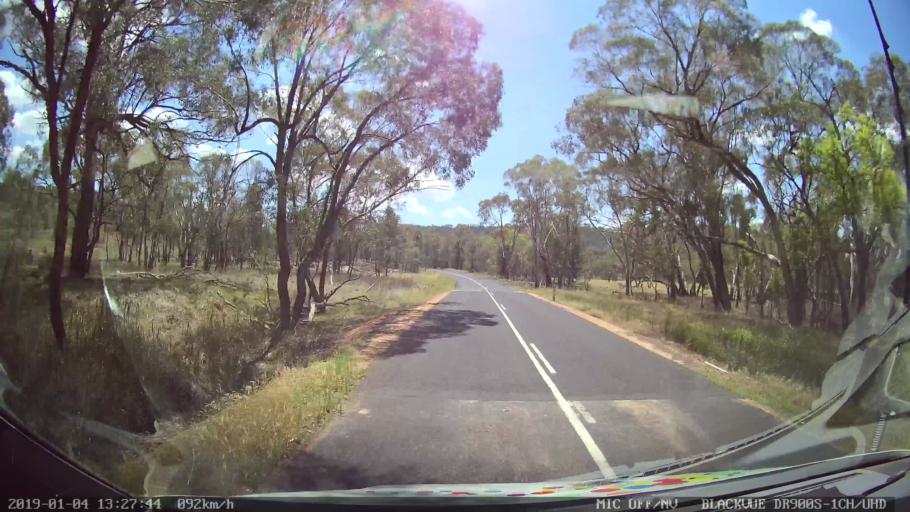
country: AU
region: New South Wales
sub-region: Parkes
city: Peak Hill
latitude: -32.6646
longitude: 148.5594
